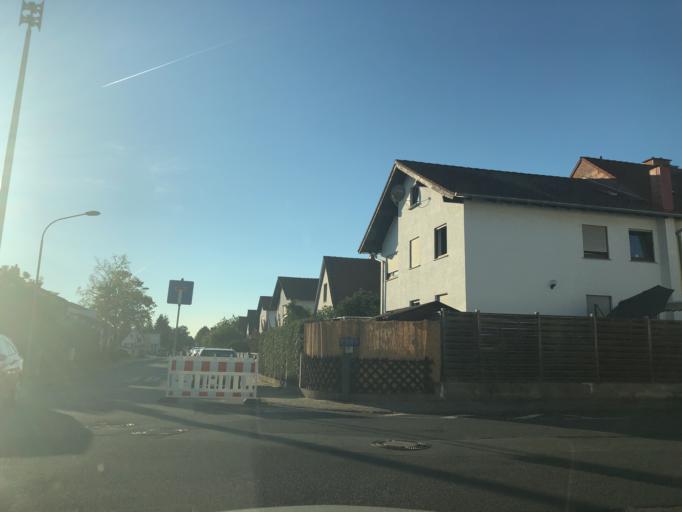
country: DE
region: Hesse
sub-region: Regierungsbezirk Darmstadt
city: Gross-Gerau
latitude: 49.9334
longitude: 8.4962
